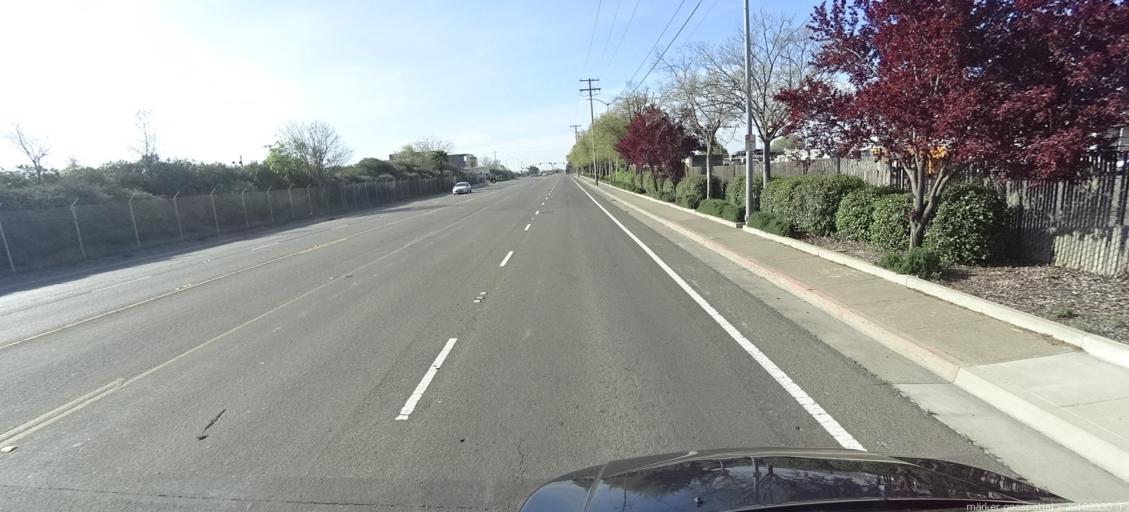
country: US
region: California
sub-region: Sacramento County
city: La Riviera
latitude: 38.5471
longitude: -121.3351
